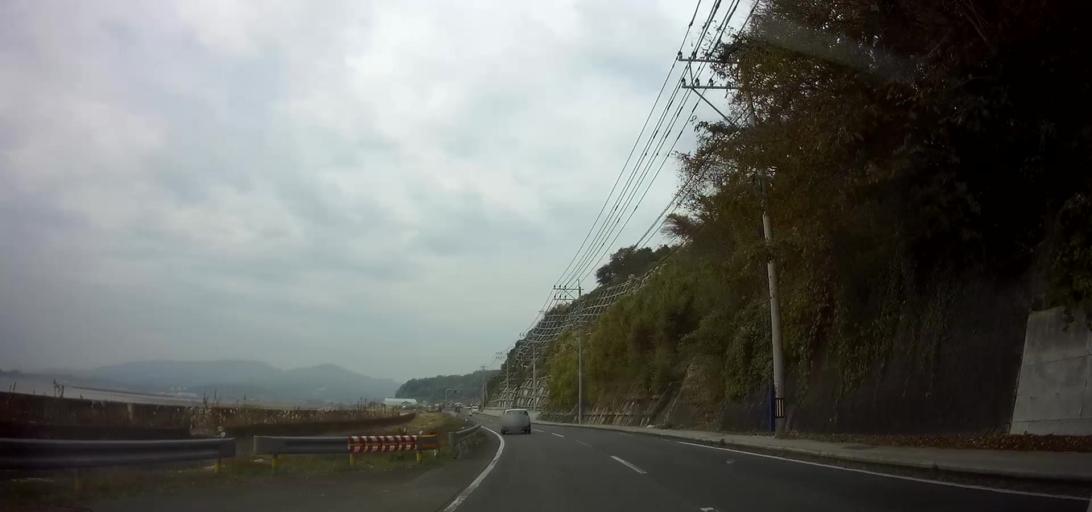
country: JP
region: Nagasaki
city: Shimabara
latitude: 32.6541
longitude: 130.2763
